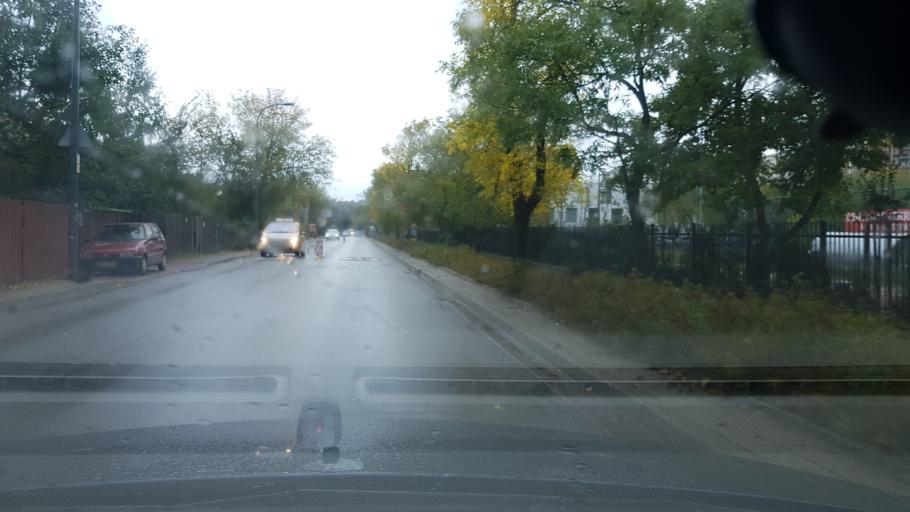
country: PL
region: Masovian Voivodeship
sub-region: Warszawa
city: Zoliborz
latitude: 52.2806
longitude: 20.9733
